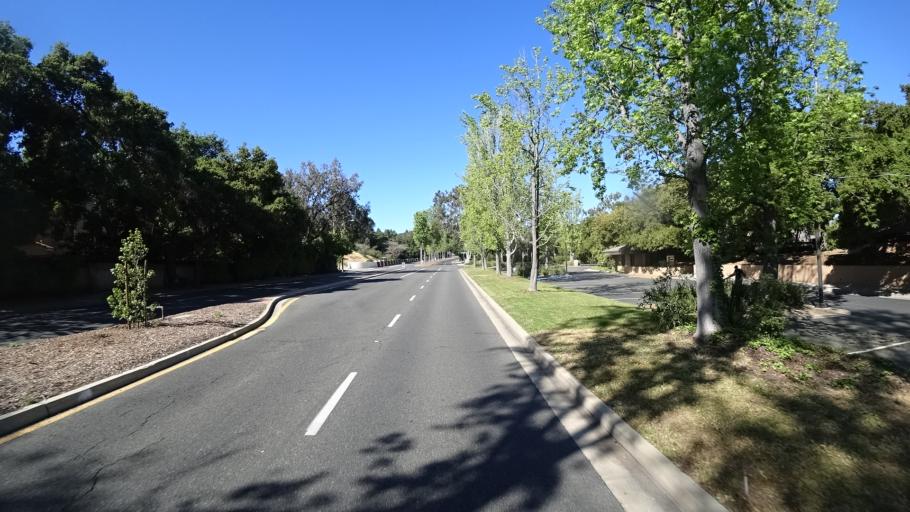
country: US
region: California
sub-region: Ventura County
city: Thousand Oaks
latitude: 34.1735
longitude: -118.8768
